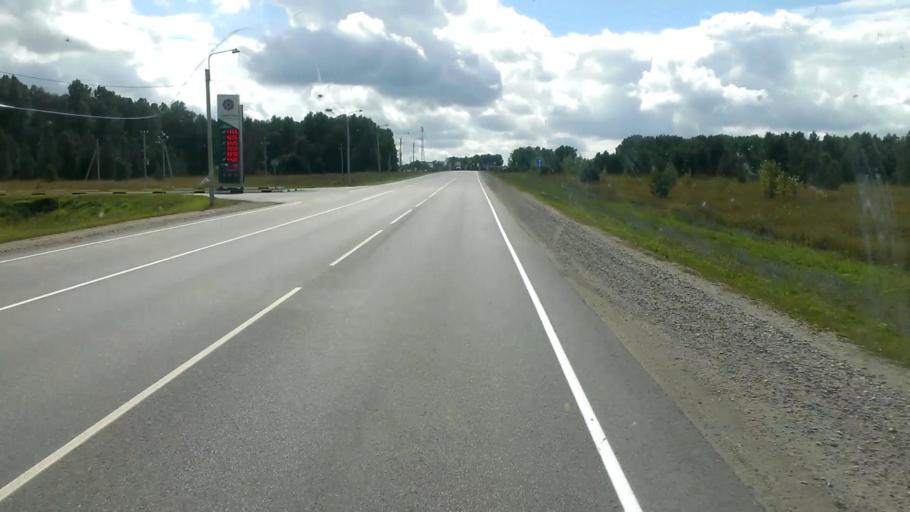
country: RU
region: Altai Krai
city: Troitskoye
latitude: 52.9745
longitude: 84.7471
